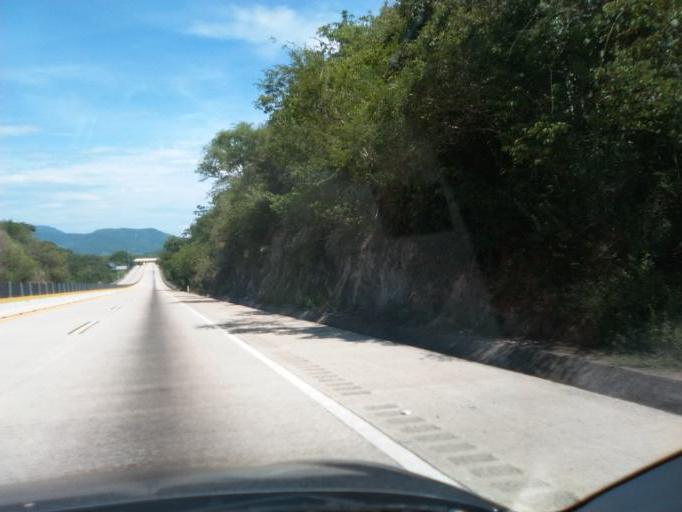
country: MX
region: Guerrero
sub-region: Acapulco de Juarez
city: Kilometro 30
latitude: 16.9659
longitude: -99.7333
